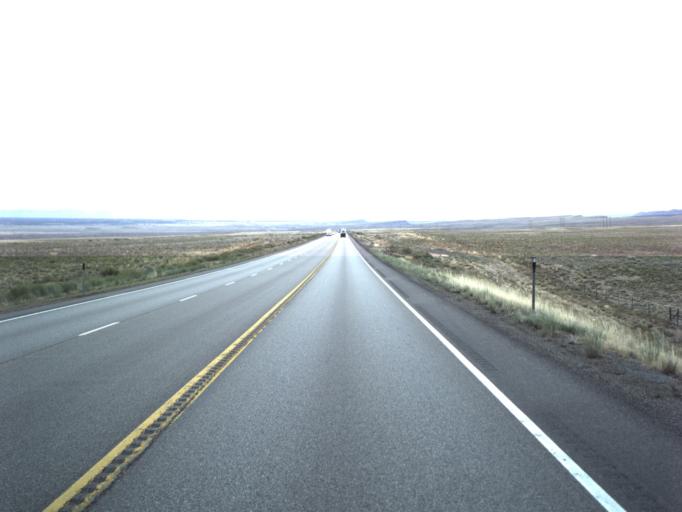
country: US
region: Utah
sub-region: Carbon County
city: East Carbon City
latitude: 39.4992
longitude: -110.5263
